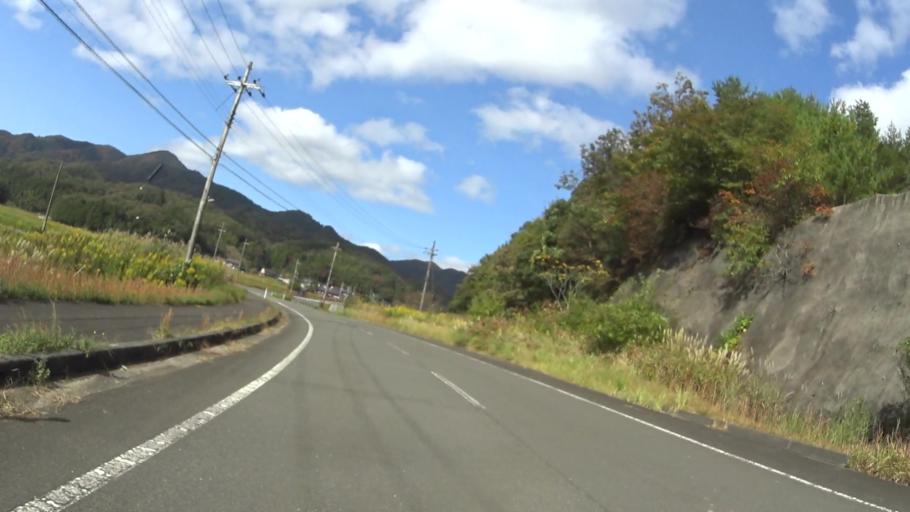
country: JP
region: Hyogo
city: Toyooka
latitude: 35.5034
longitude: 134.9925
